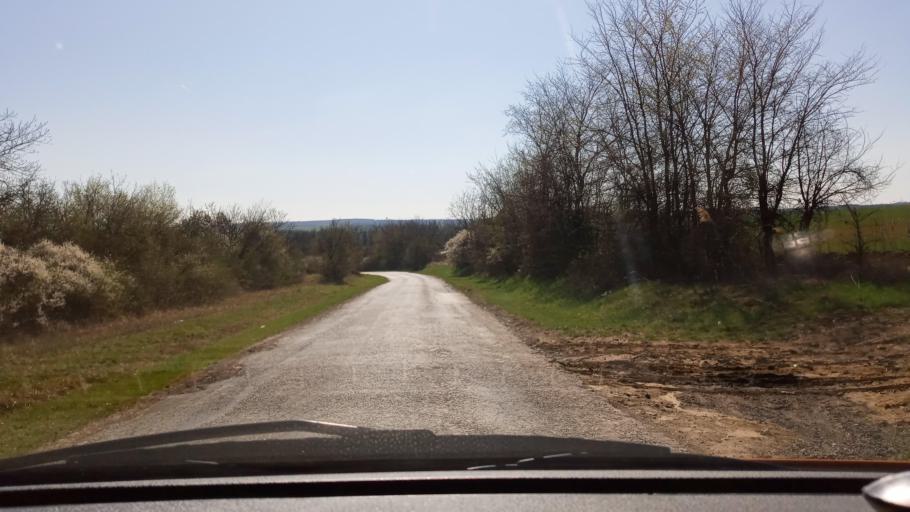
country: HU
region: Baranya
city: Kozarmisleny
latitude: 46.0741
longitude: 18.3572
